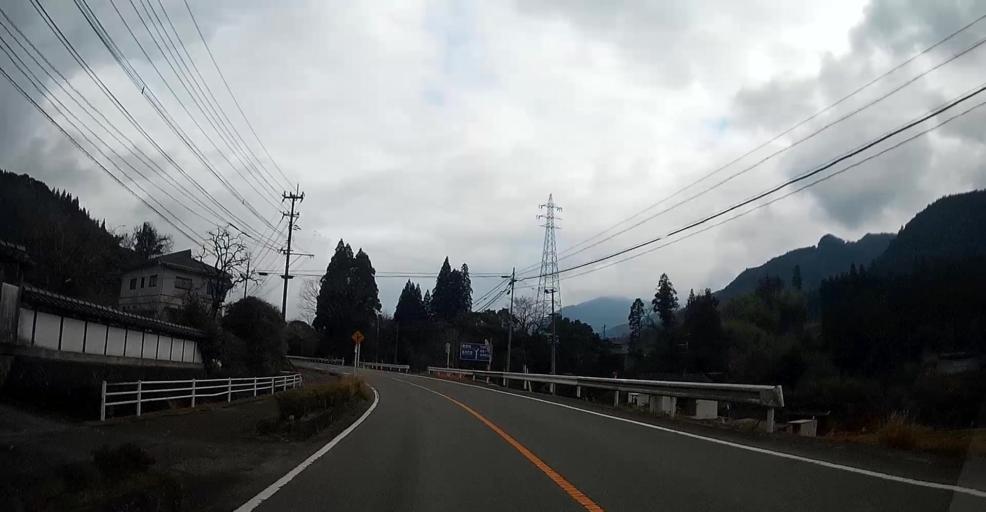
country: JP
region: Kumamoto
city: Matsubase
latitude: 32.6159
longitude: 130.8523
